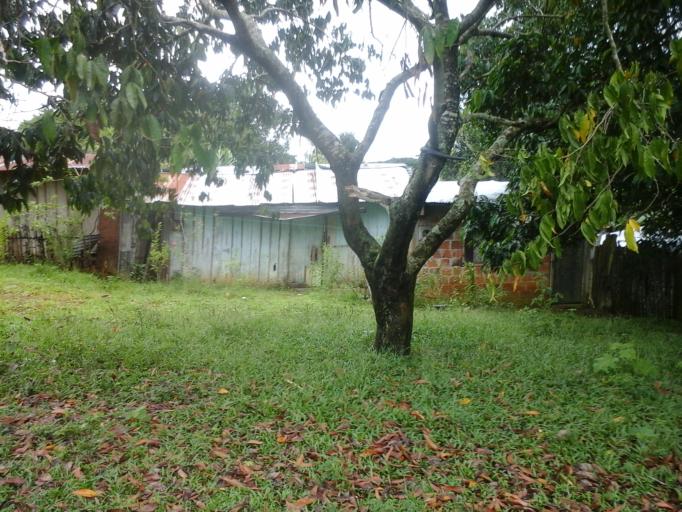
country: CO
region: Caqueta
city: El Doncello
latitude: 1.6098
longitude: -74.9991
